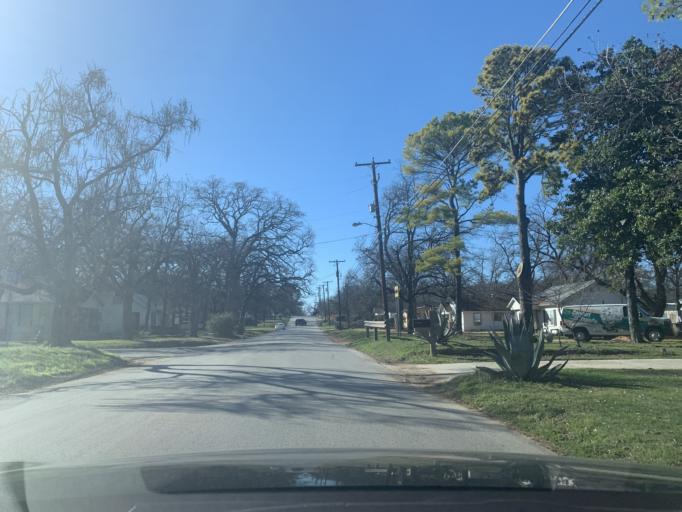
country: US
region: Texas
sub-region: Tarrant County
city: Haltom City
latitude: 32.7816
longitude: -97.2780
